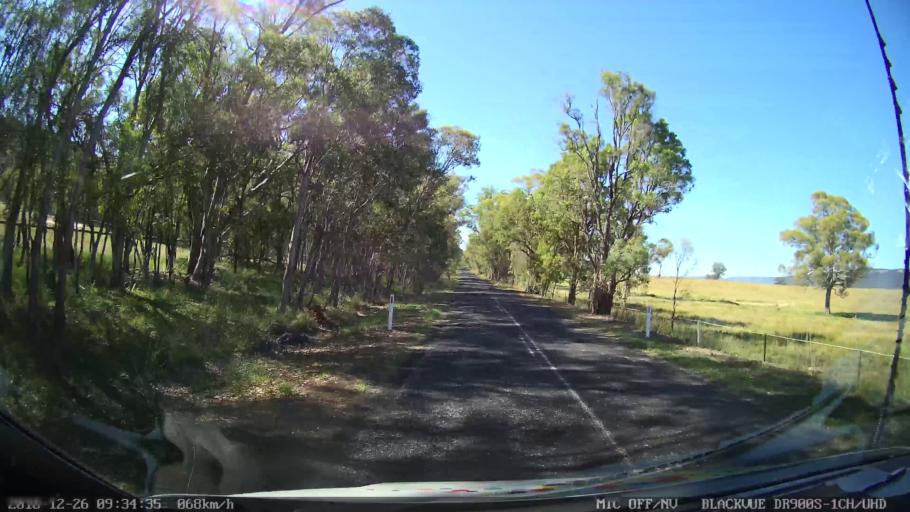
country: AU
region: New South Wales
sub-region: Mid-Western Regional
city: Kandos
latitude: -32.9068
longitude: 150.0379
